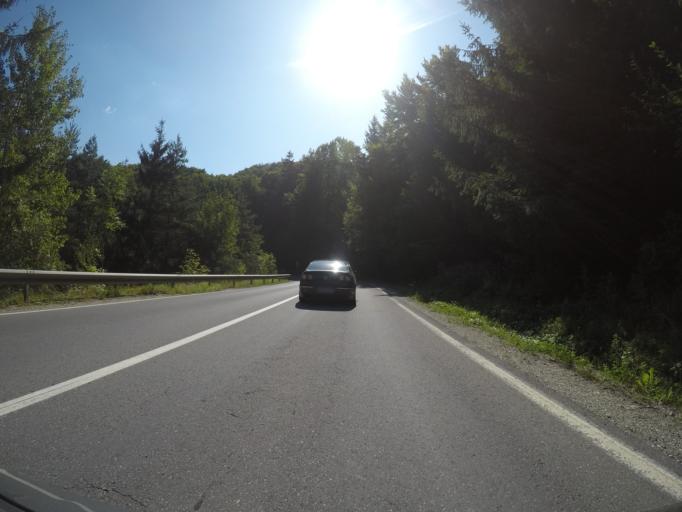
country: RO
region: Brasov
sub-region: Comuna Cristian
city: Cristian
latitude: 45.5833
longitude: 25.5051
